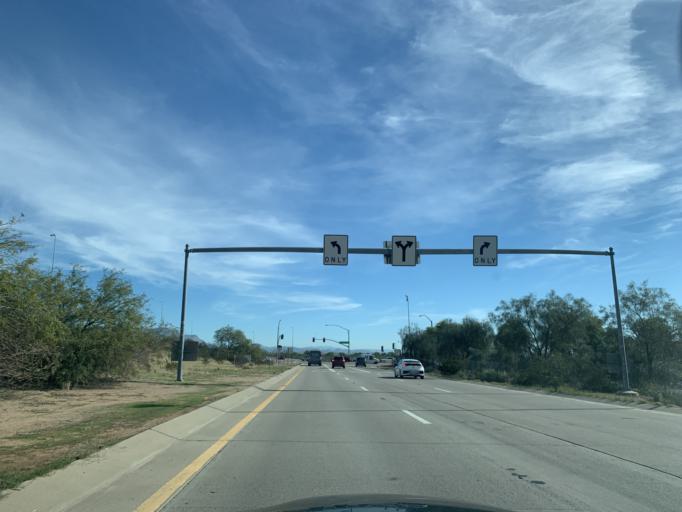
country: US
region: Arizona
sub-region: Pinal County
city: Apache Junction
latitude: 33.3861
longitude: -111.5995
